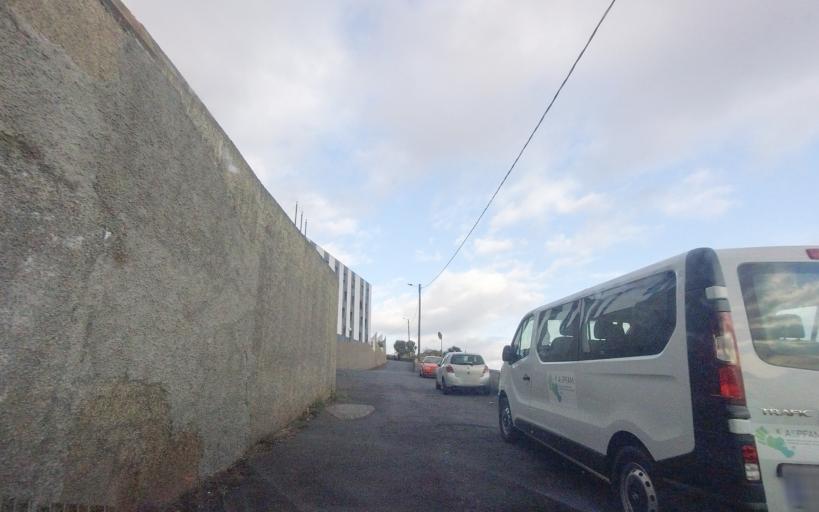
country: PT
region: Madeira
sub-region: Funchal
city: Funchal
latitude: 32.6466
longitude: -16.8850
